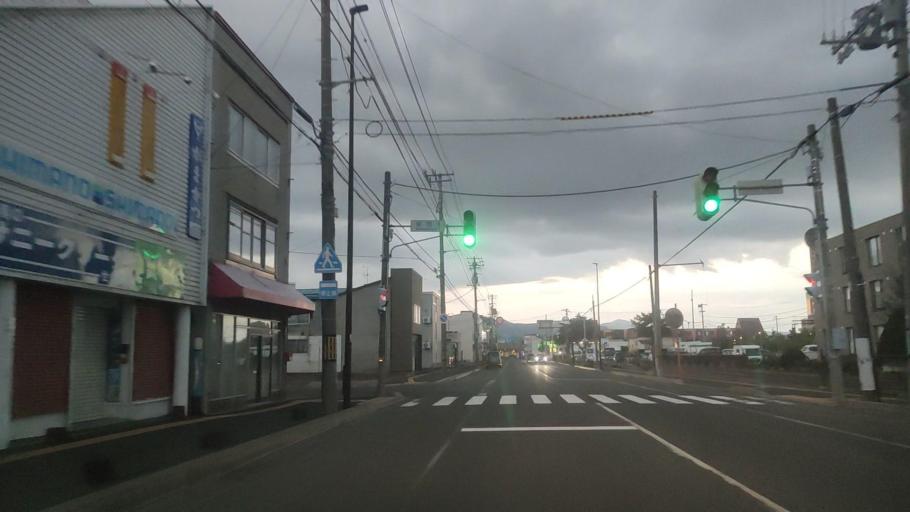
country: JP
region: Hokkaido
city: Shimo-furano
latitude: 43.3440
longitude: 142.3923
